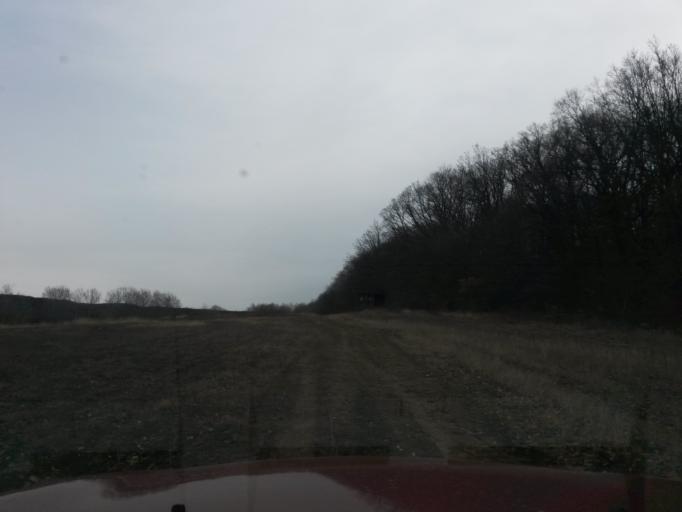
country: HU
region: Borsod-Abauj-Zemplen
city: Gonc
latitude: 48.5777
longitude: 21.3801
